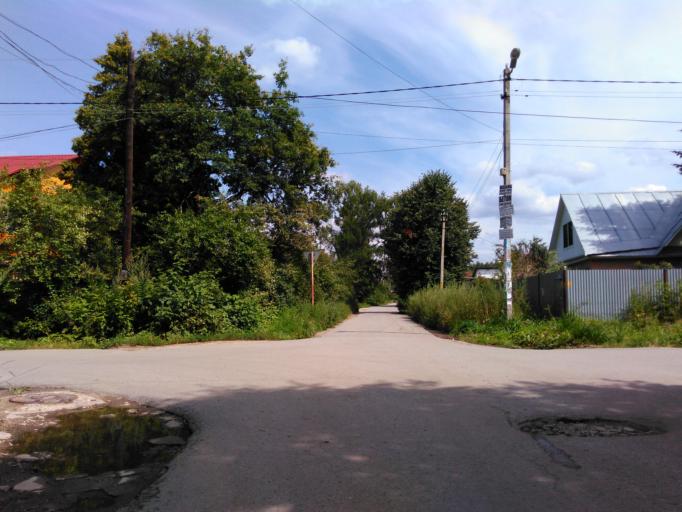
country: RU
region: Moskovskaya
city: Pravdinskiy
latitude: 56.0557
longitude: 37.8462
